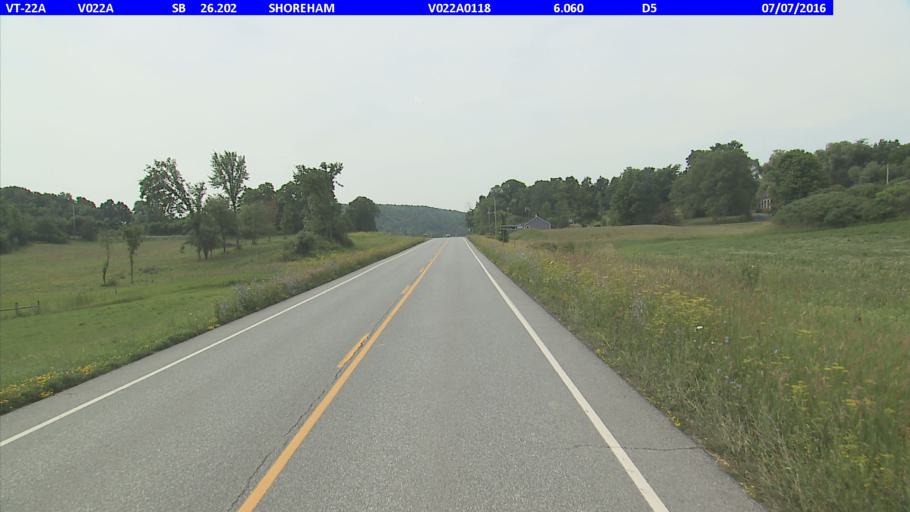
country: US
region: New York
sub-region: Essex County
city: Ticonderoga
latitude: 43.9362
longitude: -73.3103
